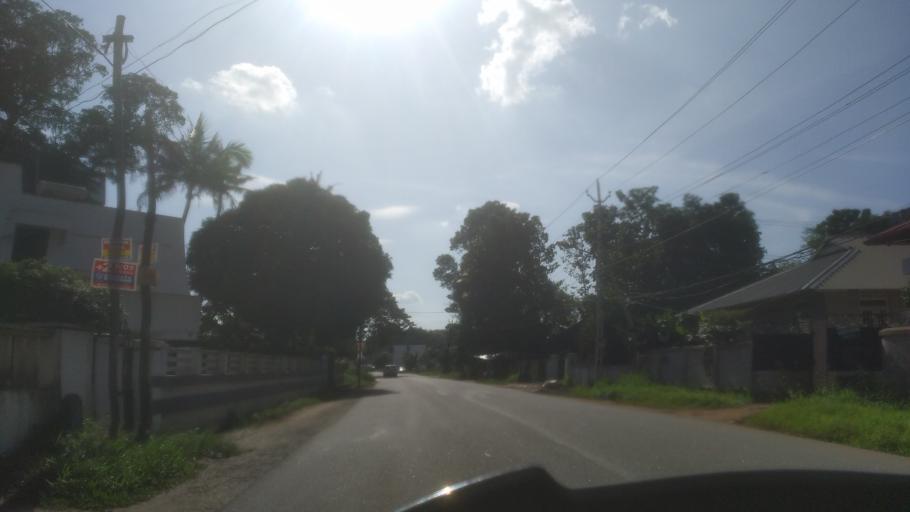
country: IN
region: Kerala
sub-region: Ernakulam
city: Muvattupuzha
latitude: 9.9855
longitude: 76.5644
